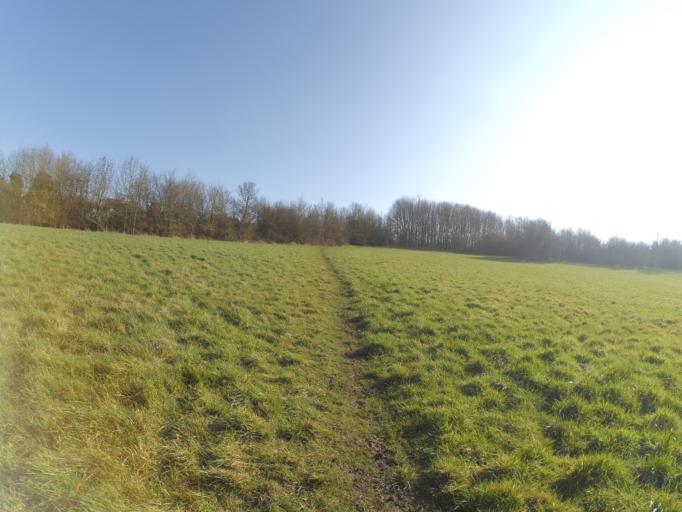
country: GB
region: England
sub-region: Greater London
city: Wembley
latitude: 51.5755
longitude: -0.2701
